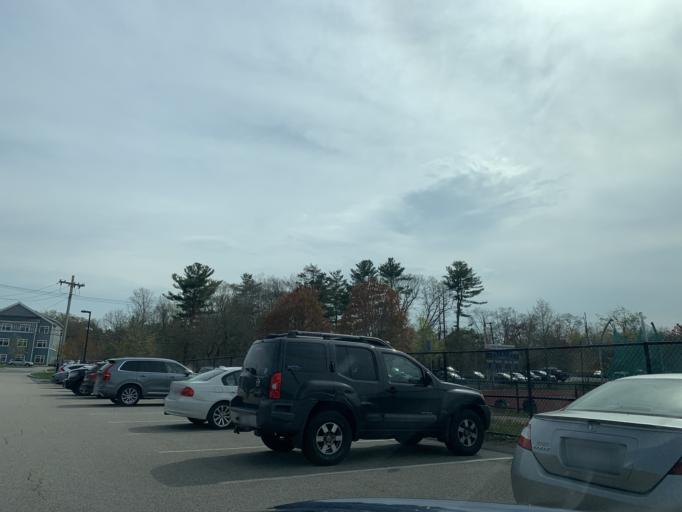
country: US
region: Massachusetts
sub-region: Norfolk County
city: Norwood
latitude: 42.2146
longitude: -71.1939
